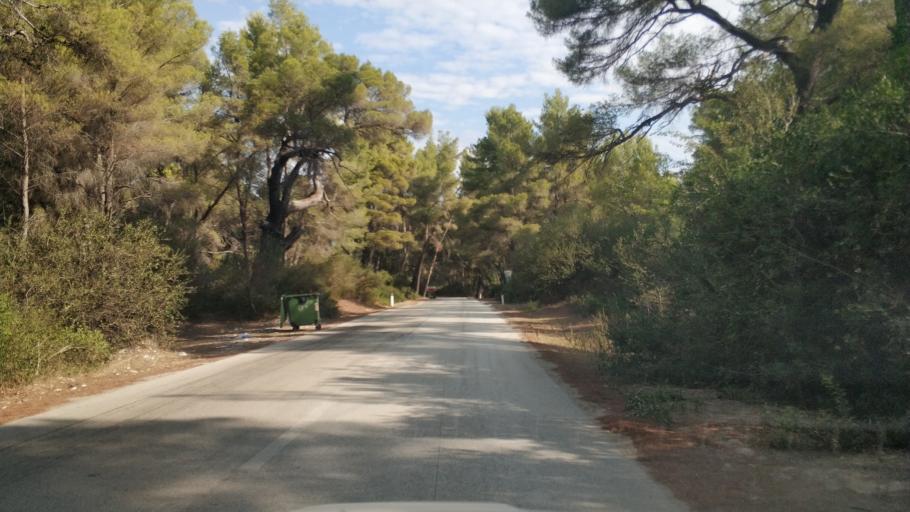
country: AL
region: Fier
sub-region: Rrethi i Lushnjes
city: Divjake
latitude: 40.9807
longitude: 19.4822
